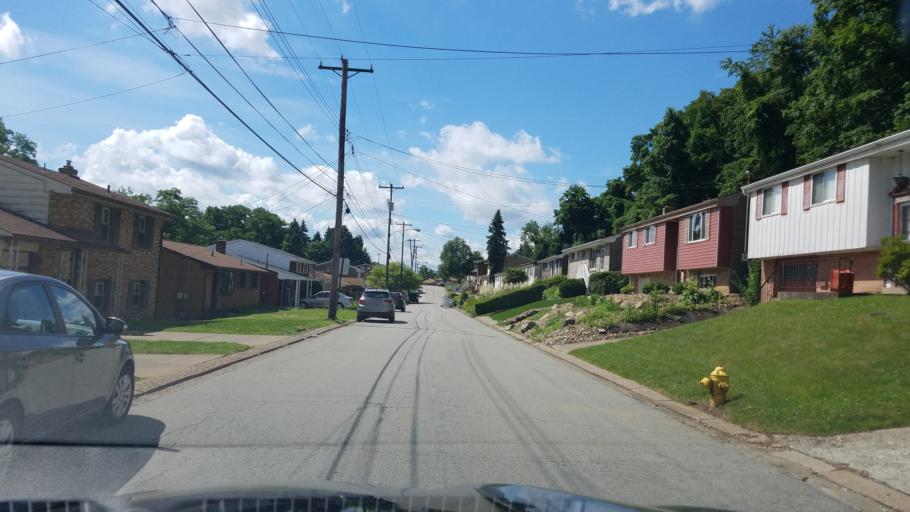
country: US
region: Pennsylvania
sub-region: Allegheny County
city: Rankin
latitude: 40.4180
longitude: -79.8734
